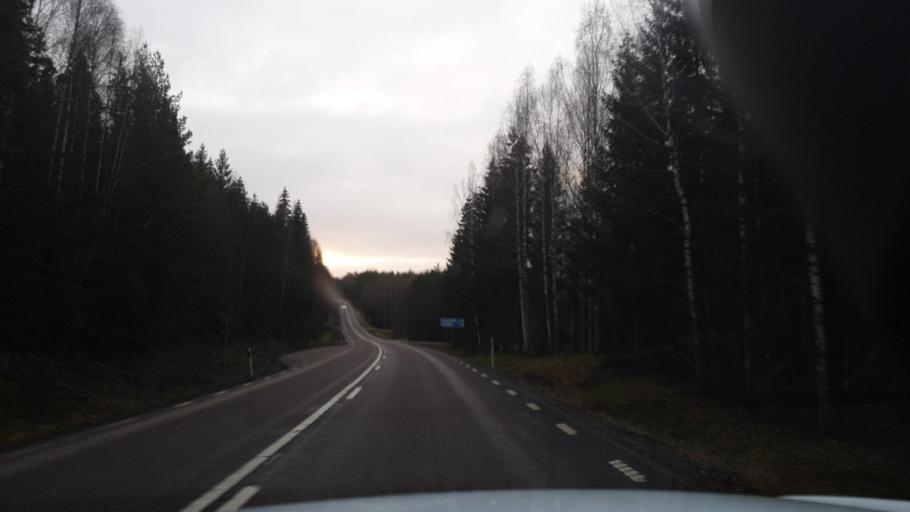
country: SE
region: Vaermland
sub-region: Arvika Kommun
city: Arvika
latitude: 59.7168
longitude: 12.5275
